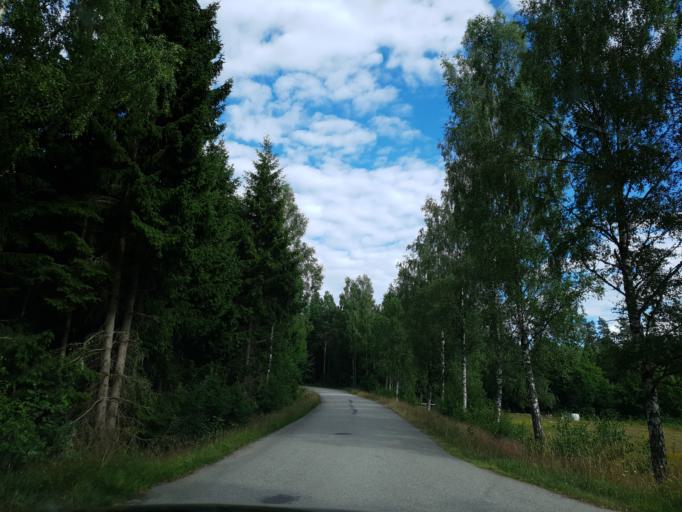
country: SE
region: Kalmar
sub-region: Emmaboda Kommun
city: Emmaboda
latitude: 56.6234
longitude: 15.6468
